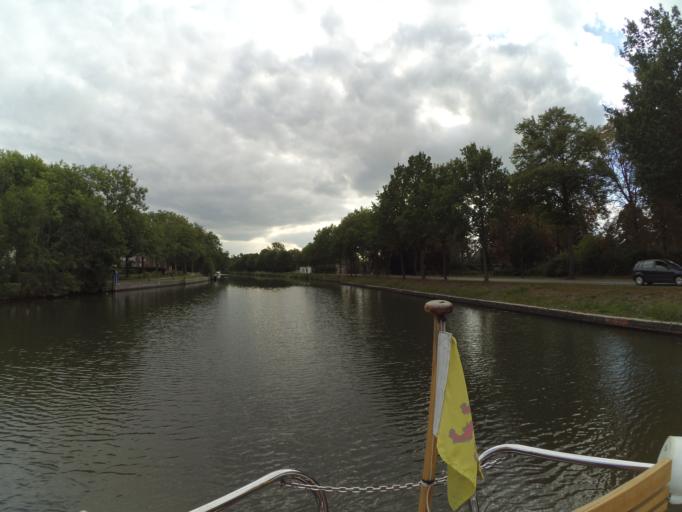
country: NL
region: Utrecht
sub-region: Stichtse Vecht
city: Maarssen
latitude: 52.1451
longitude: 5.0316
